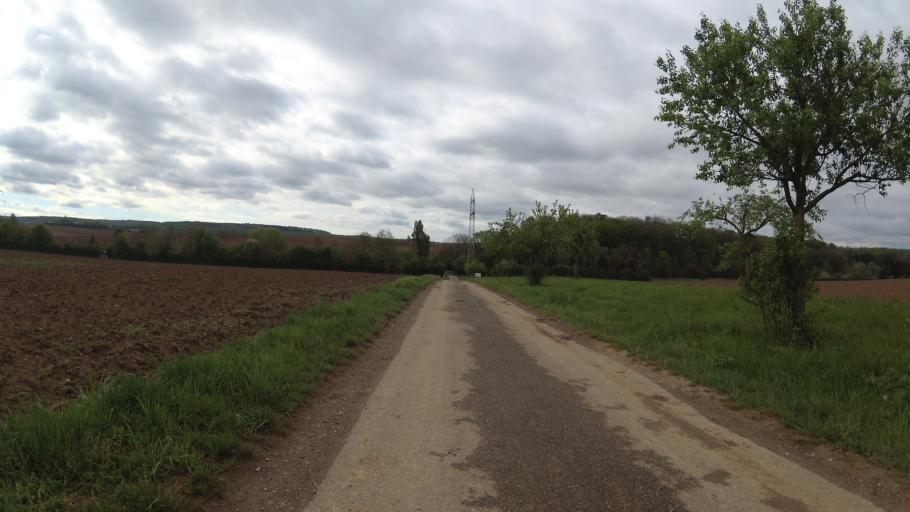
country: DE
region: Baden-Wuerttemberg
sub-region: Regierungsbezirk Stuttgart
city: Oedheim
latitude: 49.2222
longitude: 9.2599
